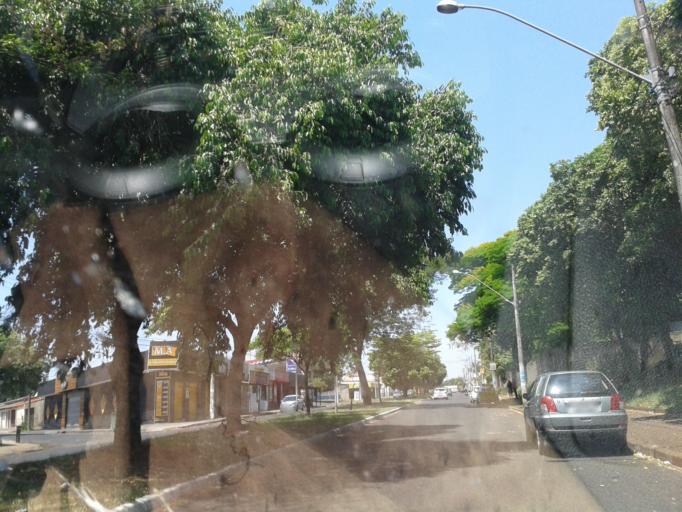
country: BR
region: Minas Gerais
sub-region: Uberlandia
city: Uberlandia
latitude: -18.9351
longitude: -48.3048
